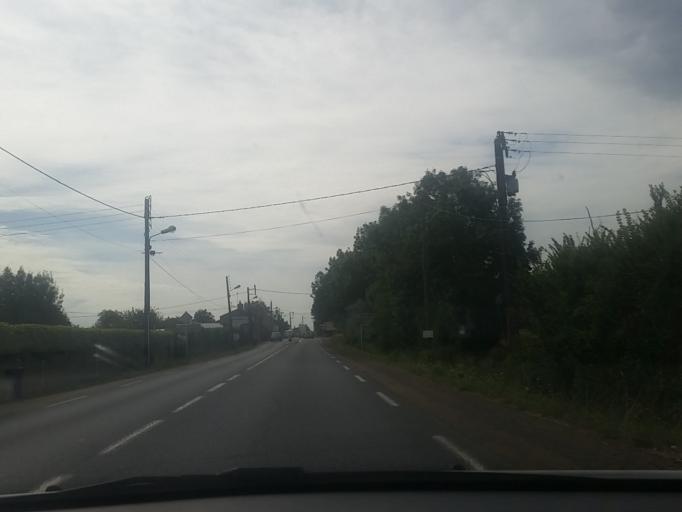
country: FR
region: Pays de la Loire
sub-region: Departement de la Vendee
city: Sainte-Cecile
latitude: 46.7441
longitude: -1.0893
